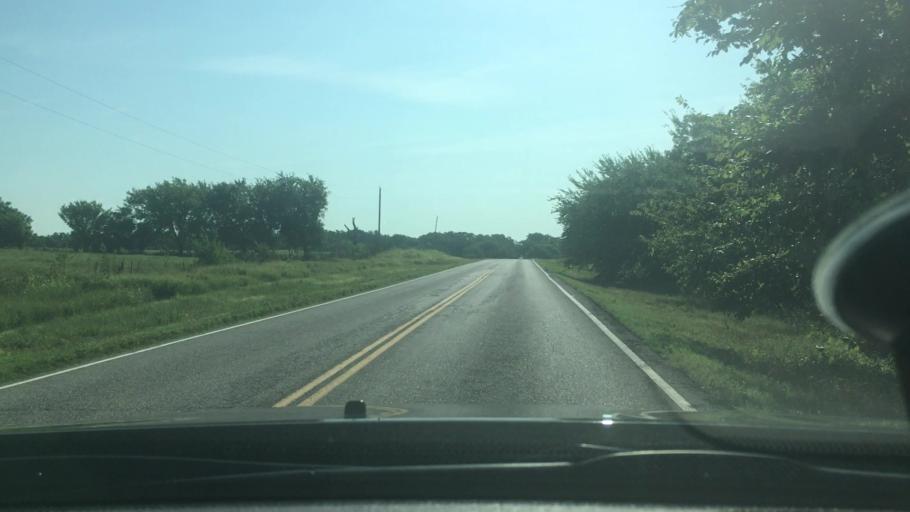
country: US
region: Oklahoma
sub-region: Garvin County
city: Pauls Valley
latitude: 34.6520
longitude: -97.3126
